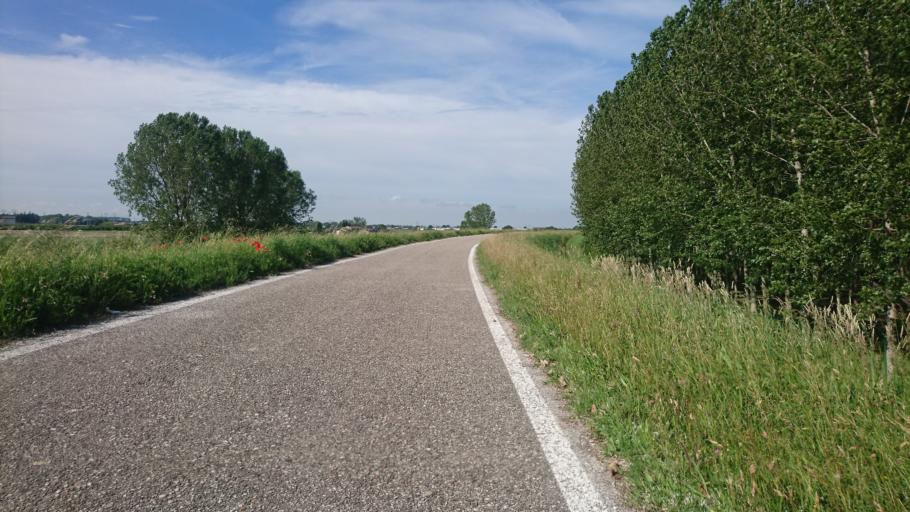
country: IT
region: Veneto
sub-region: Provincia di Rovigo
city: Bergantino
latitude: 45.0399
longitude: 11.2507
